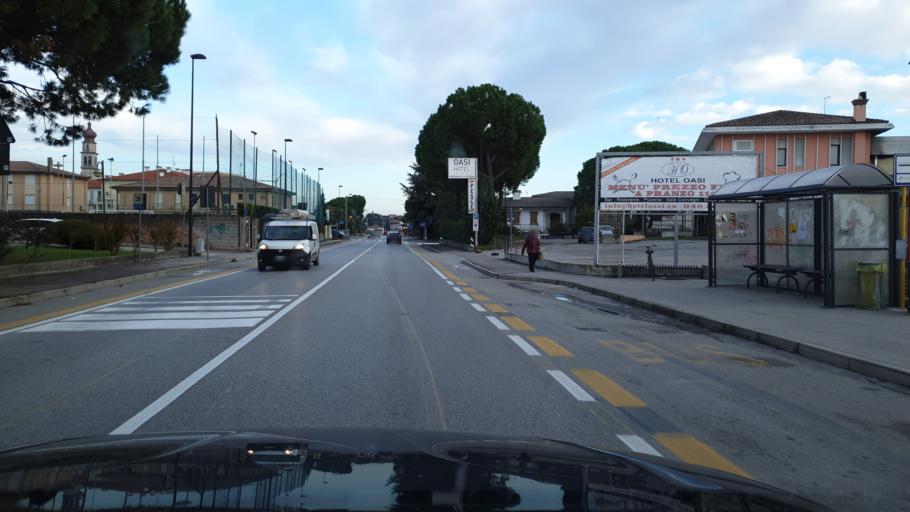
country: IT
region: Veneto
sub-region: Provincia di Padova
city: Conselve
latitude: 45.2321
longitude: 11.8704
